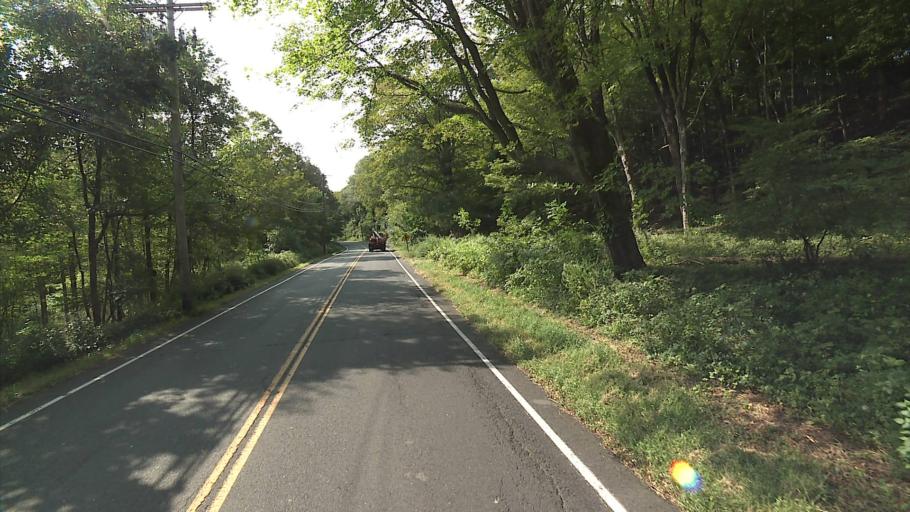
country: US
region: Connecticut
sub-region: Fairfield County
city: Georgetown
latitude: 41.2524
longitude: -73.3234
